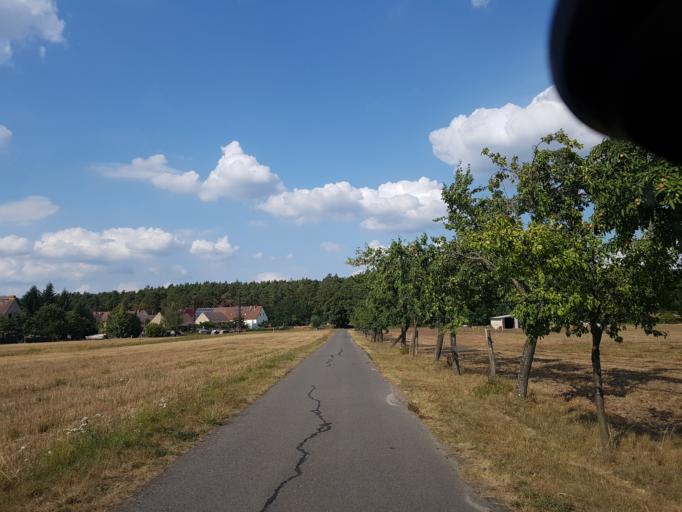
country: DE
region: Brandenburg
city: Calau
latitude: 51.7743
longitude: 13.9586
